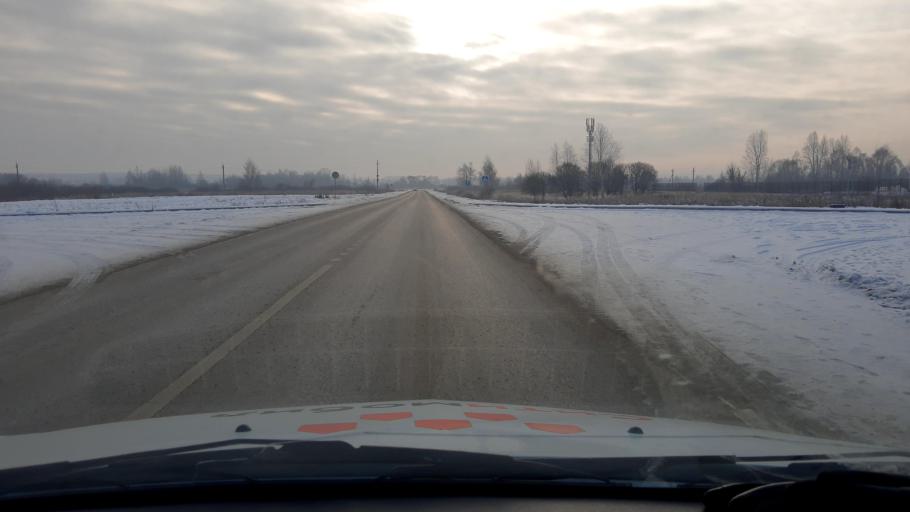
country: RU
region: Bashkortostan
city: Kabakovo
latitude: 54.7389
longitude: 56.2029
